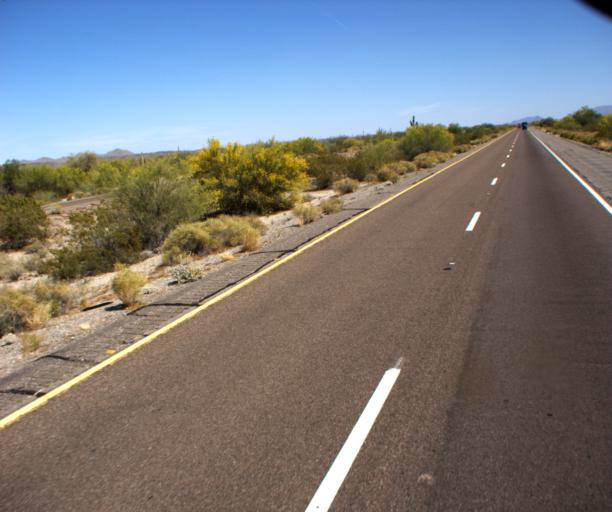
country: US
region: Arizona
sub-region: Maricopa County
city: Gila Bend
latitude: 32.8580
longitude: -112.3865
